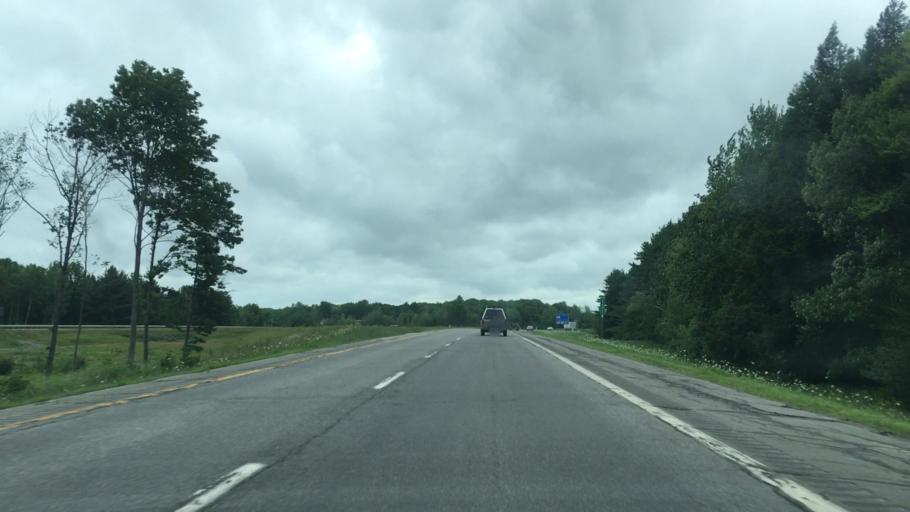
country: US
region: Maine
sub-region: Kennebec County
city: Waterville
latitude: 44.5776
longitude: -69.6302
